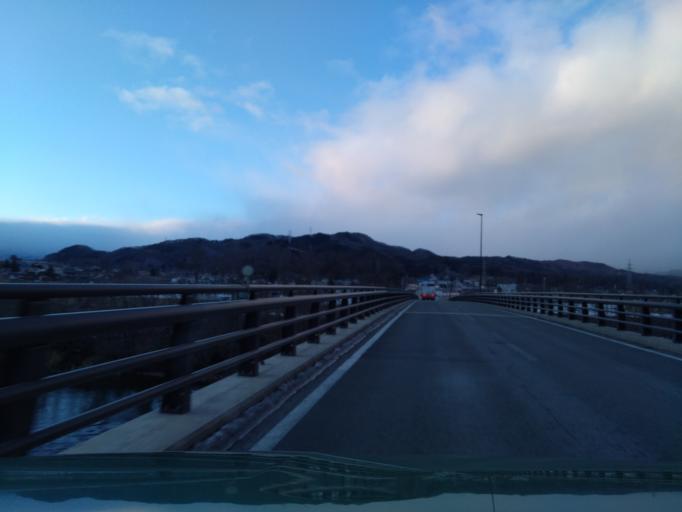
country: JP
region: Iwate
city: Shizukuishi
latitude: 39.6965
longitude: 141.0640
